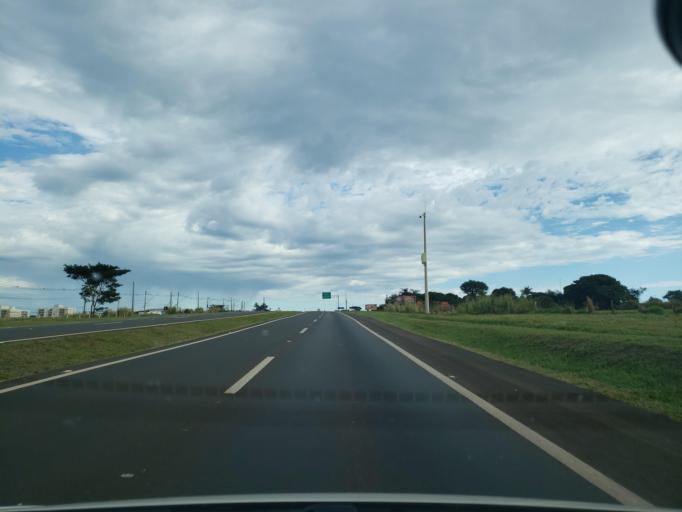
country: BR
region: Sao Paulo
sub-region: Jau
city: Jau
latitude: -22.2585
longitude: -48.5444
